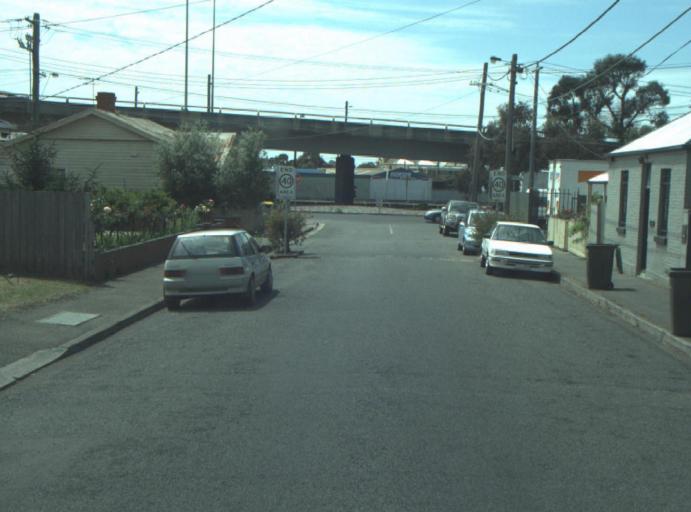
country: AU
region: Victoria
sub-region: Greater Geelong
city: Geelong West
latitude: -38.1404
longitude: 144.3528
